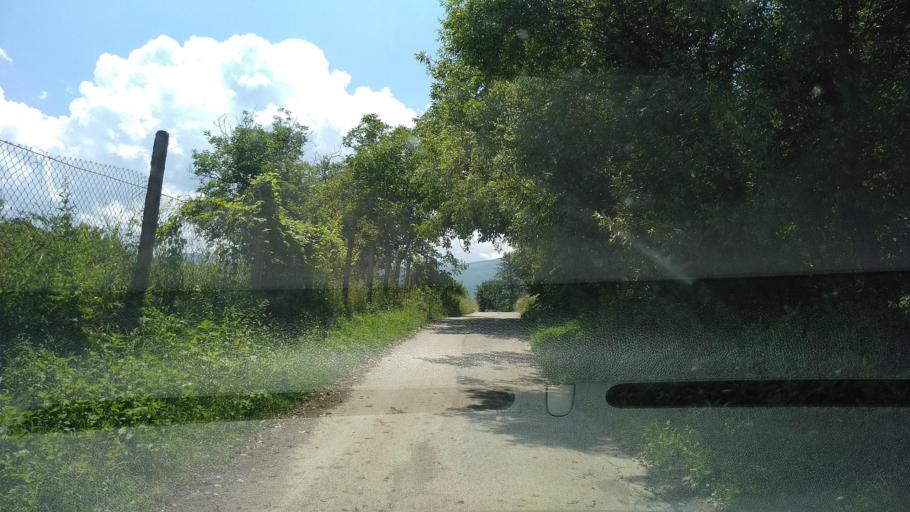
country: RO
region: Hunedoara
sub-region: Comuna Sarmizegetusa
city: Sarmizegetusa
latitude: 45.5431
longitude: 22.8184
